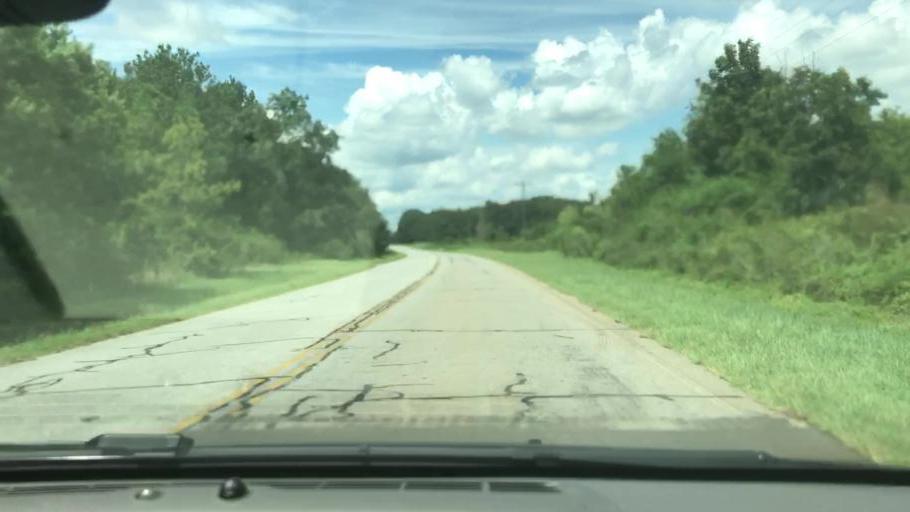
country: US
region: Georgia
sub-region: Stewart County
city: Lumpkin
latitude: 32.1337
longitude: -84.9928
